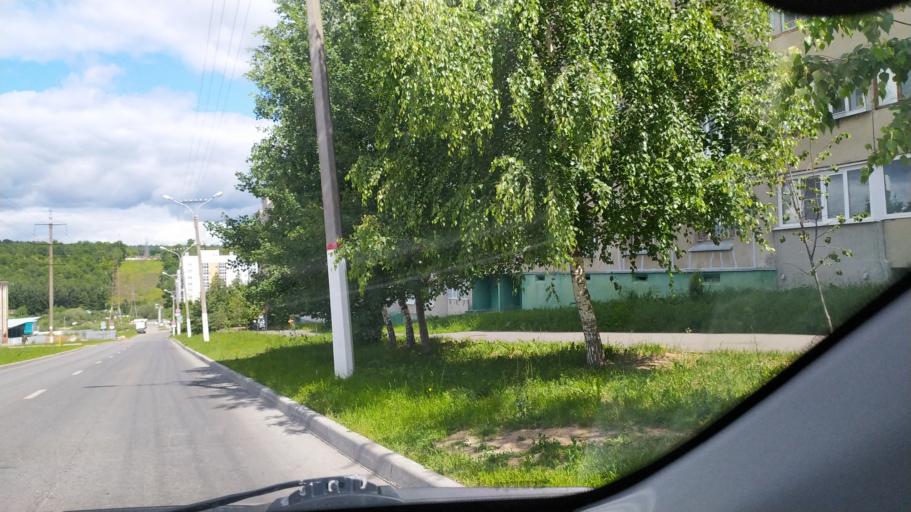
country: RU
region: Chuvashia
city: Novyye Lapsary
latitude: 56.1193
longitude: 47.1750
